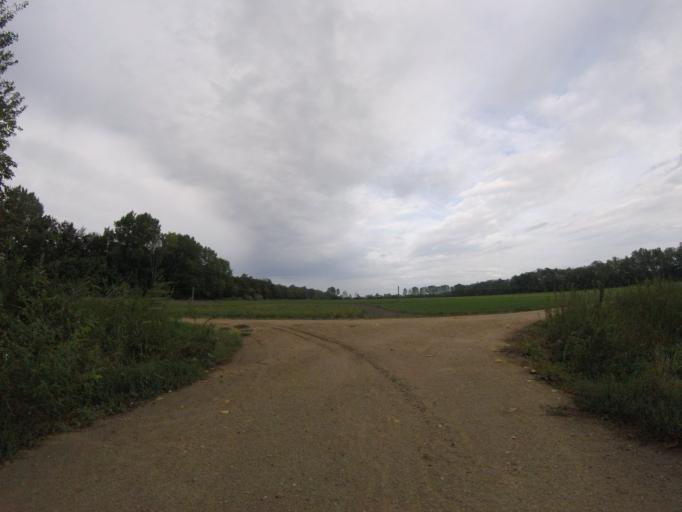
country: HU
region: Gyor-Moson-Sopron
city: Fertod
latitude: 47.6410
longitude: 16.7891
